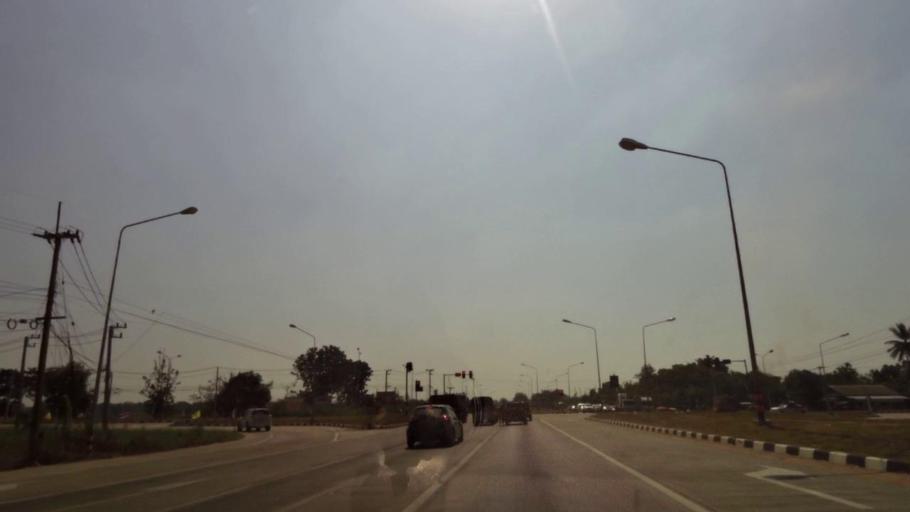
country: TH
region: Phichit
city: Wachira Barami
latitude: 16.3555
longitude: 100.1293
